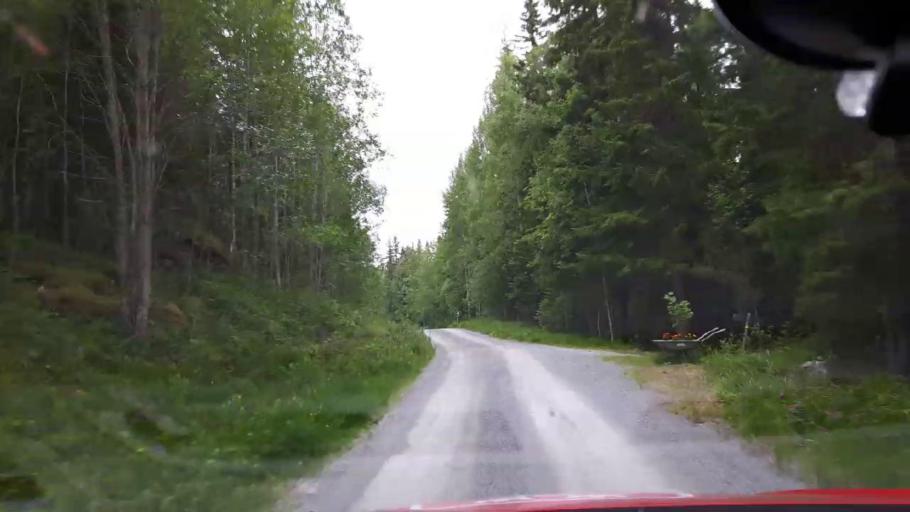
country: SE
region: Jaemtland
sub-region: OEstersunds Kommun
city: Brunflo
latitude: 63.0424
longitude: 14.9235
